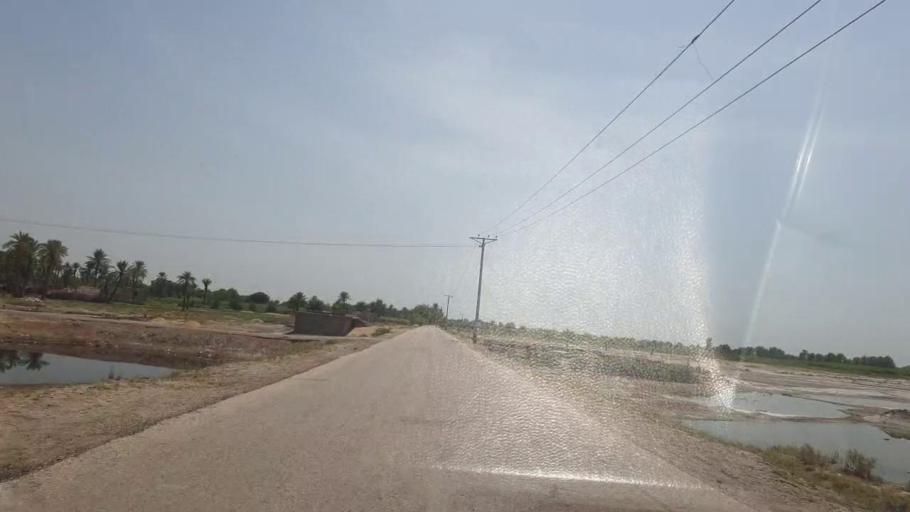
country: PK
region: Sindh
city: Bozdar
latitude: 27.0714
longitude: 68.5958
